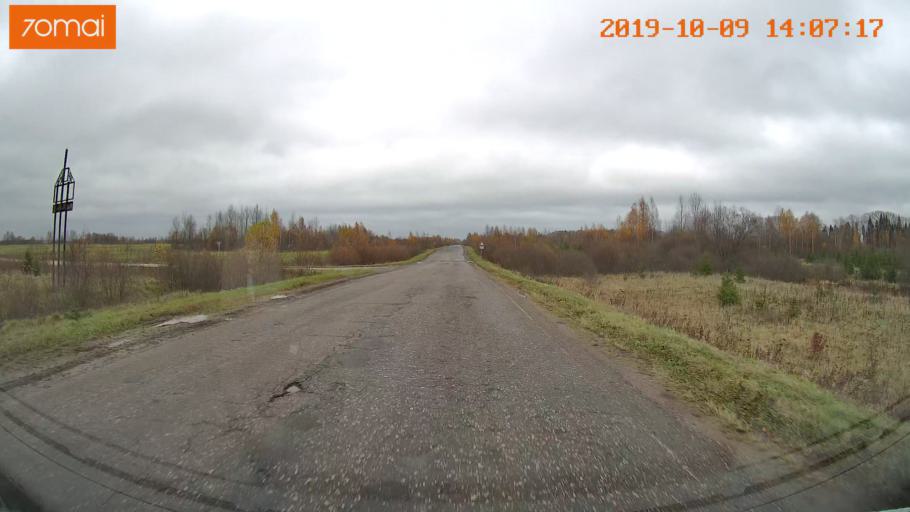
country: RU
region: Kostroma
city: Buy
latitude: 58.4696
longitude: 41.4207
